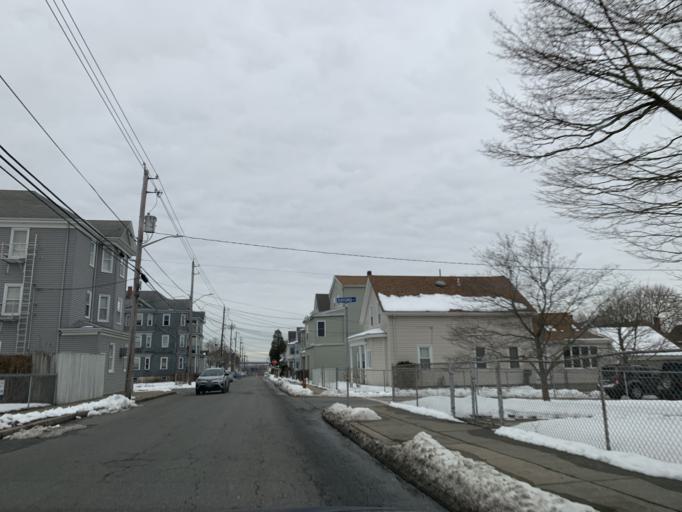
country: US
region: Massachusetts
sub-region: Bristol County
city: Fall River
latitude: 41.6881
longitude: -71.1540
